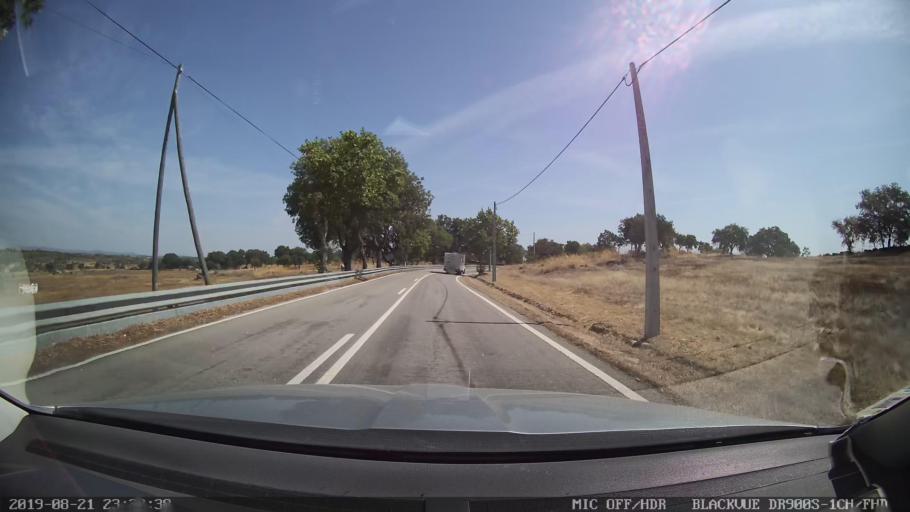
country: PT
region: Guarda
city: Alcains
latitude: 39.8801
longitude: -7.4105
